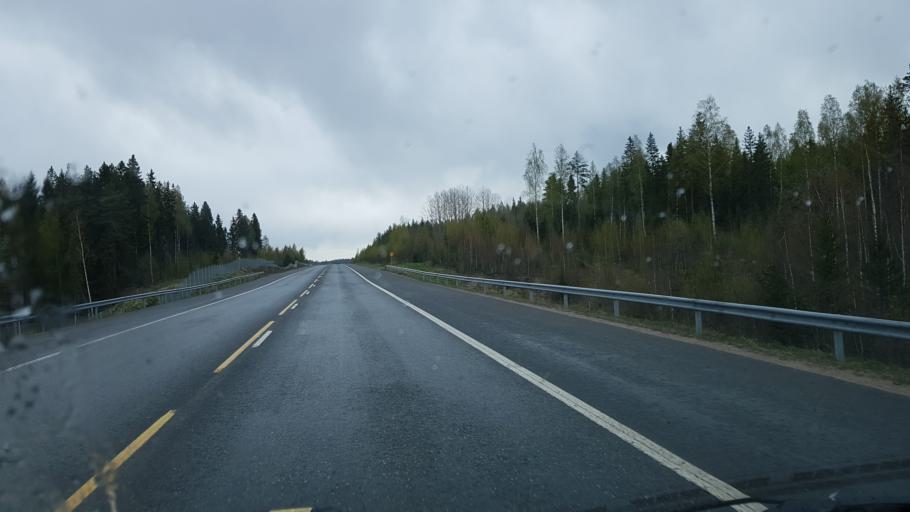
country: FI
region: Pirkanmaa
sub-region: Tampere
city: Pirkkala
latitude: 61.4106
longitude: 23.6340
